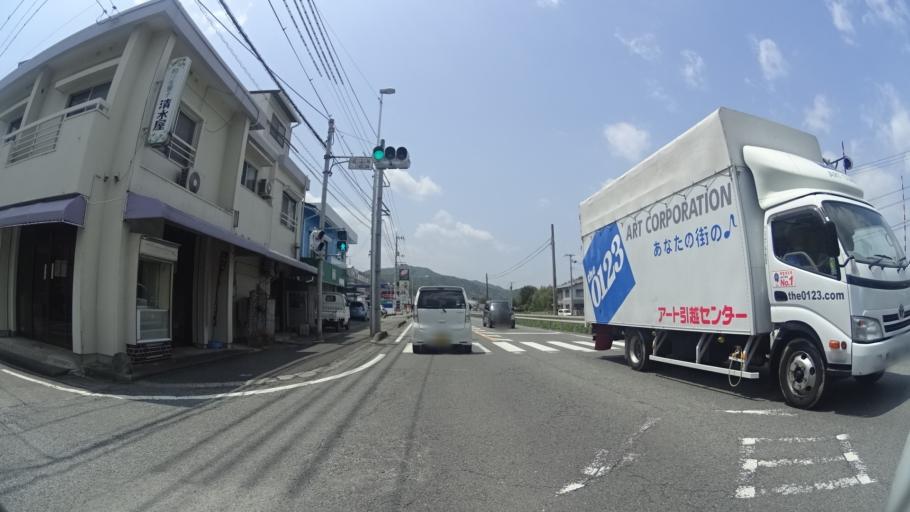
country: JP
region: Tokushima
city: Ishii
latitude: 34.0673
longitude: 134.4377
